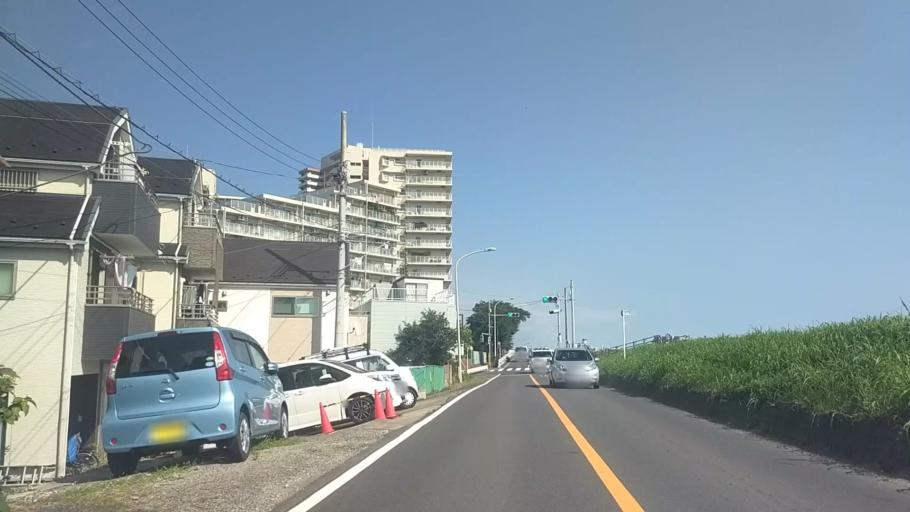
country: JP
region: Kanagawa
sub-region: Kawasaki-shi
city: Kawasaki
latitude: 35.5560
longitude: 139.7010
